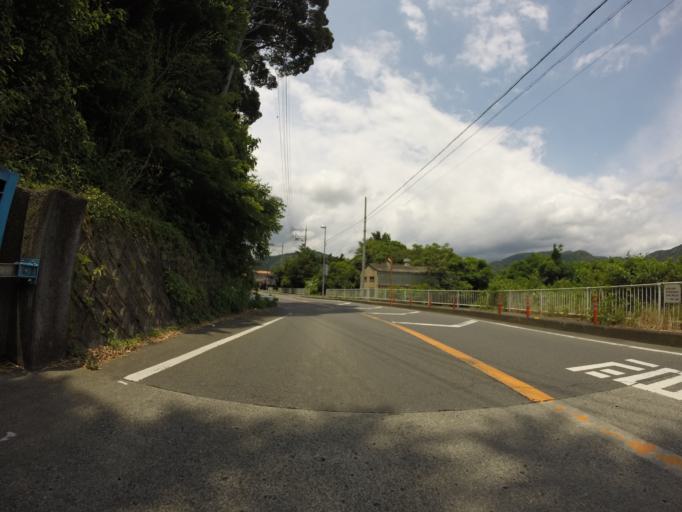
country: JP
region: Shizuoka
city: Shizuoka-shi
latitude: 34.9767
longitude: 138.3377
